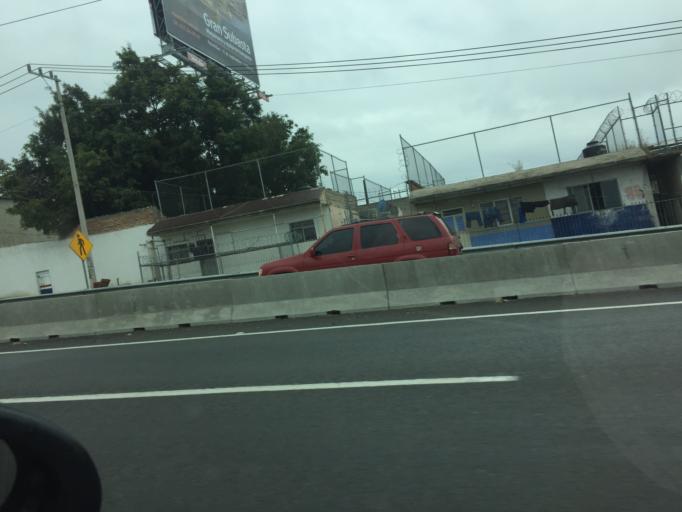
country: MX
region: Jalisco
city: Tlaquepaque
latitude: 20.6190
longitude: -103.2689
